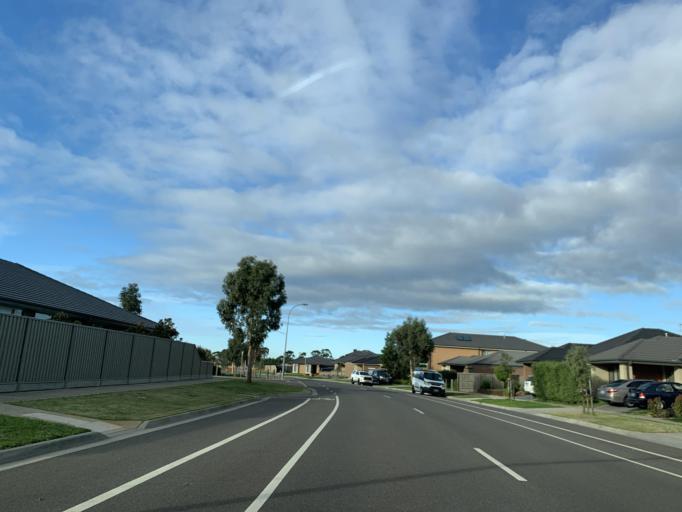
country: AU
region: Victoria
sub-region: Casey
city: Cranbourne East
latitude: -38.1260
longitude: 145.3027
